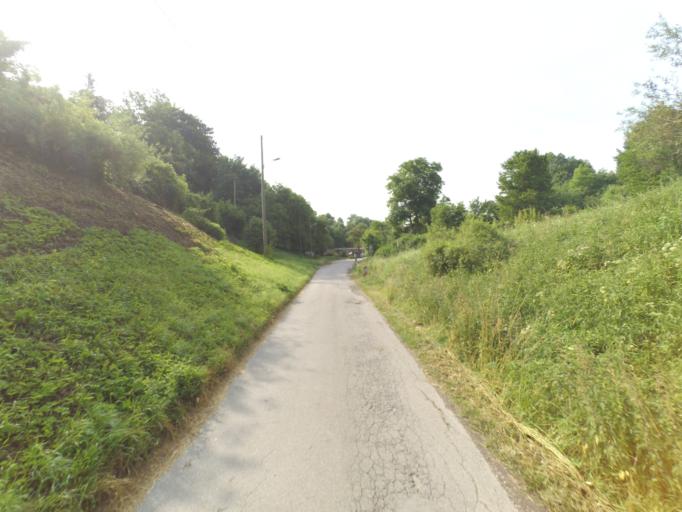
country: DE
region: Baden-Wuerttemberg
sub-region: Tuebingen Region
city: Ulm
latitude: 48.4149
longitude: 9.9946
